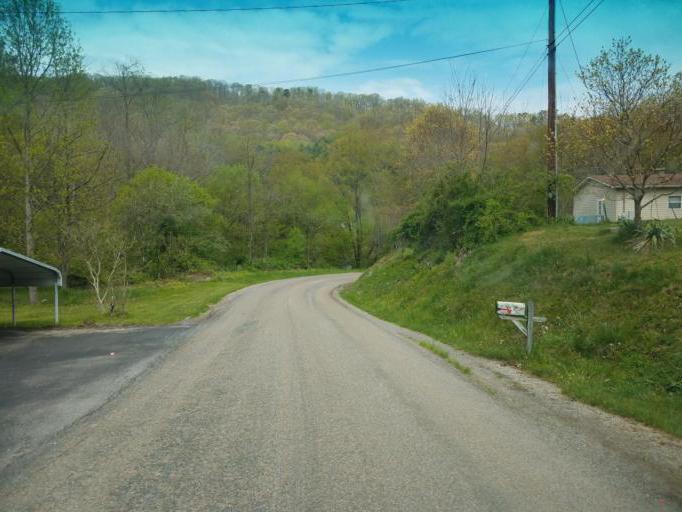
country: US
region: Virginia
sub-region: Smyth County
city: Marion
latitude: 36.8062
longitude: -81.4660
